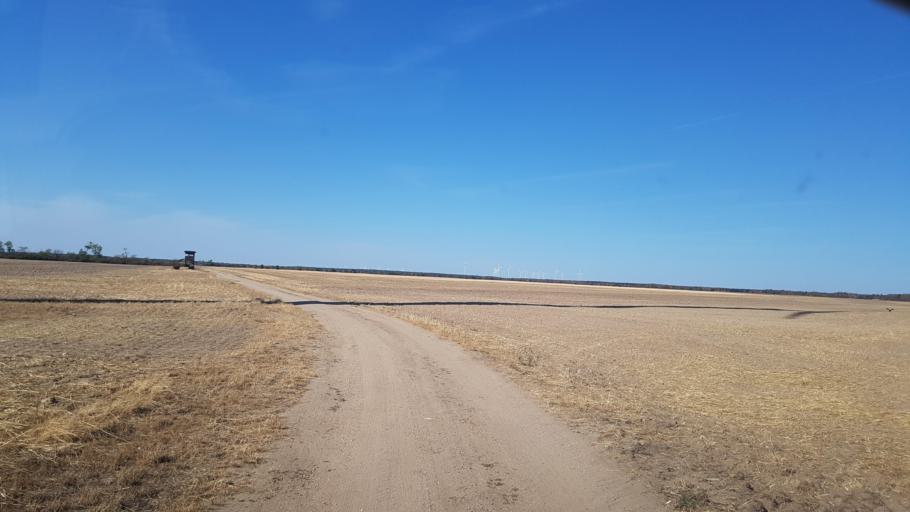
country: DE
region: Brandenburg
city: Muhlberg
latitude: 51.4112
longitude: 13.2865
